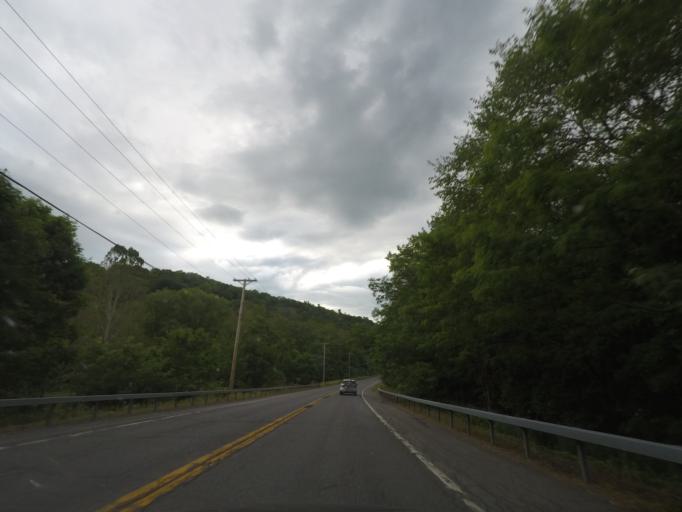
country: US
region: New York
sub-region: Dutchess County
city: Pine Plains
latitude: 41.9739
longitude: -73.6382
